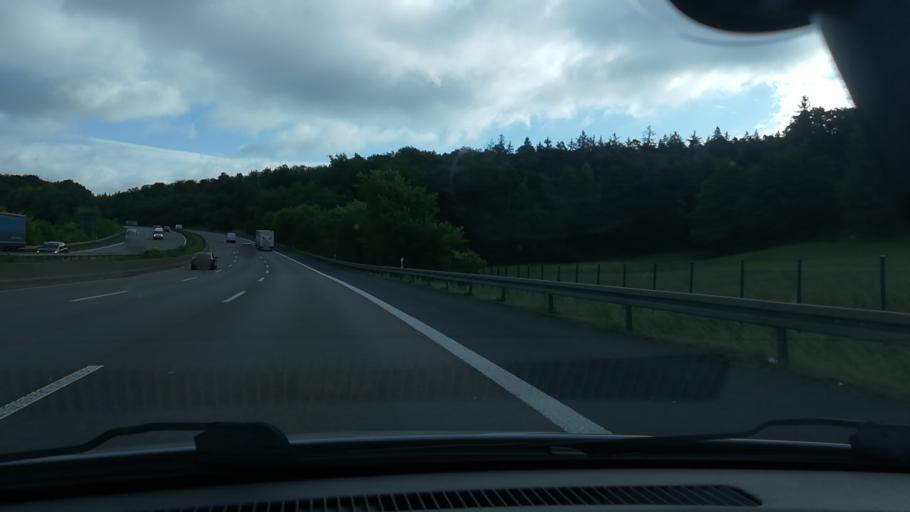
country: DE
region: Hesse
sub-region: Regierungsbezirk Kassel
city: Homberg
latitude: 51.0075
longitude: 9.4868
